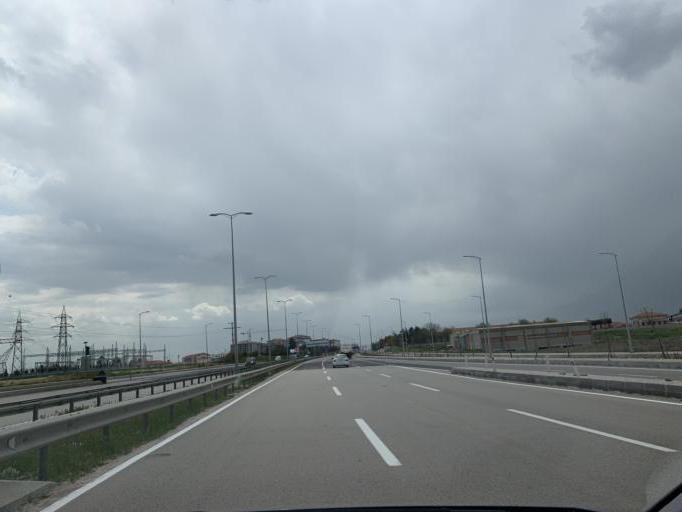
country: TR
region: Ankara
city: Polatli
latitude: 39.5858
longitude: 32.1662
